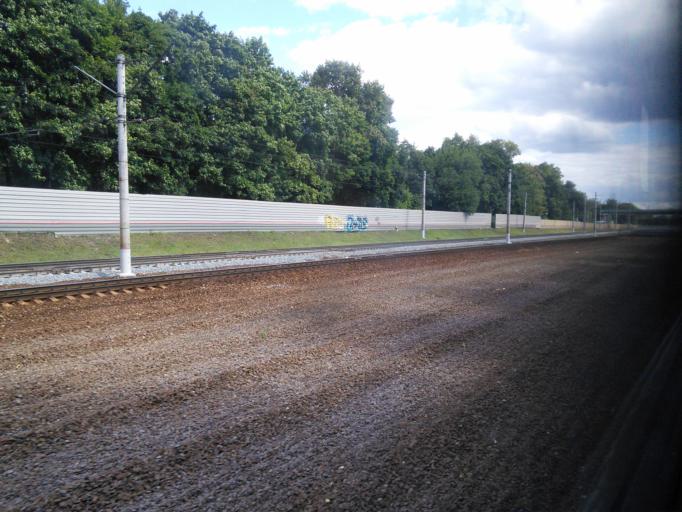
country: RU
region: Moskovskaya
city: Malakhovka
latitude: 55.6360
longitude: 38.0403
